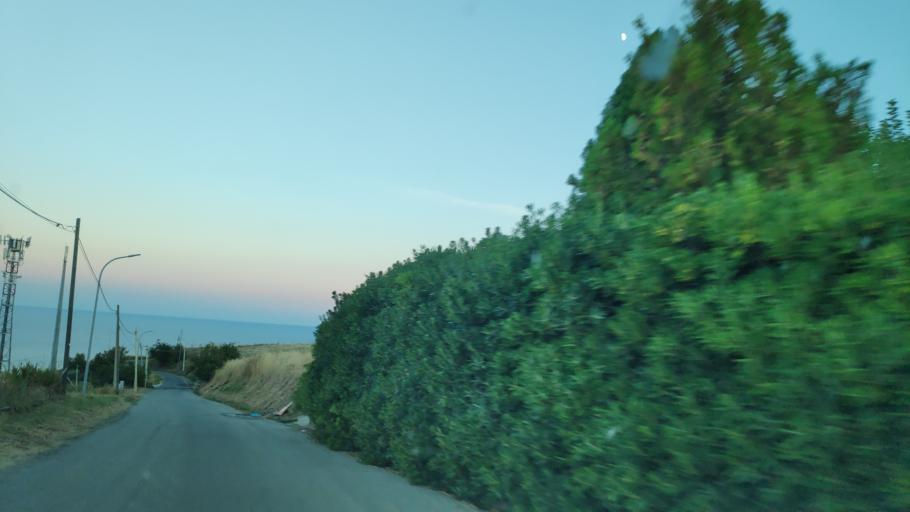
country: IT
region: Calabria
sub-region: Provincia di Reggio Calabria
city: Riace Marina
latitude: 38.3954
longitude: 16.5245
